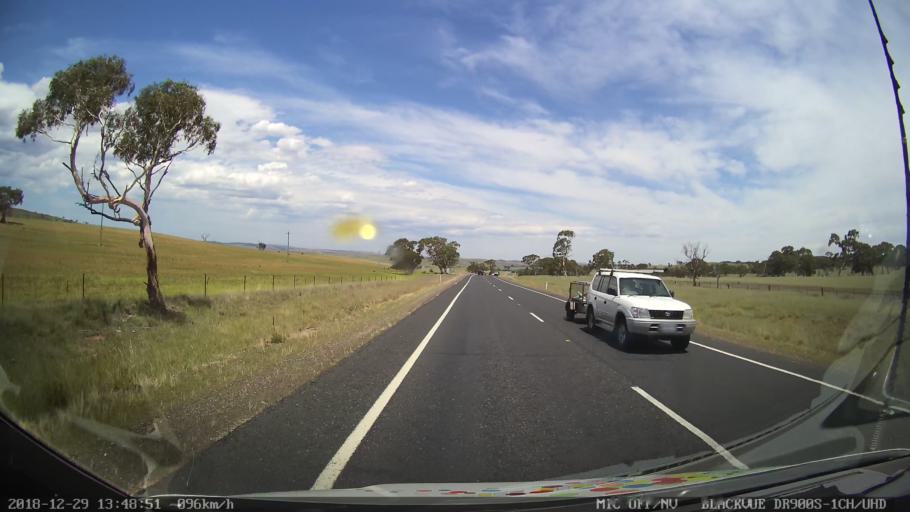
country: AU
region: New South Wales
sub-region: Cooma-Monaro
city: Cooma
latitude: -36.1458
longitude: 149.1496
